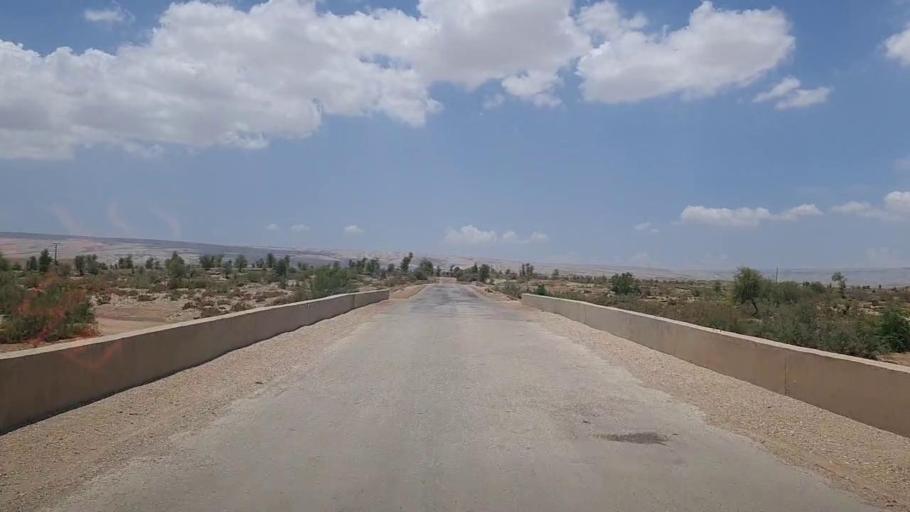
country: PK
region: Sindh
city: Sehwan
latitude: 26.3209
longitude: 67.6520
